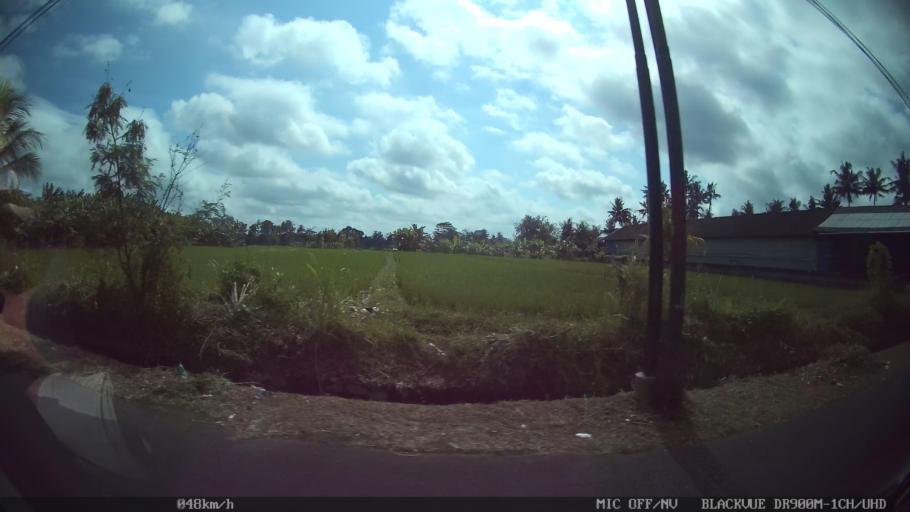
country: ID
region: Bali
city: Banjar Pesalakan
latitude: -8.5186
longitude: 115.3118
